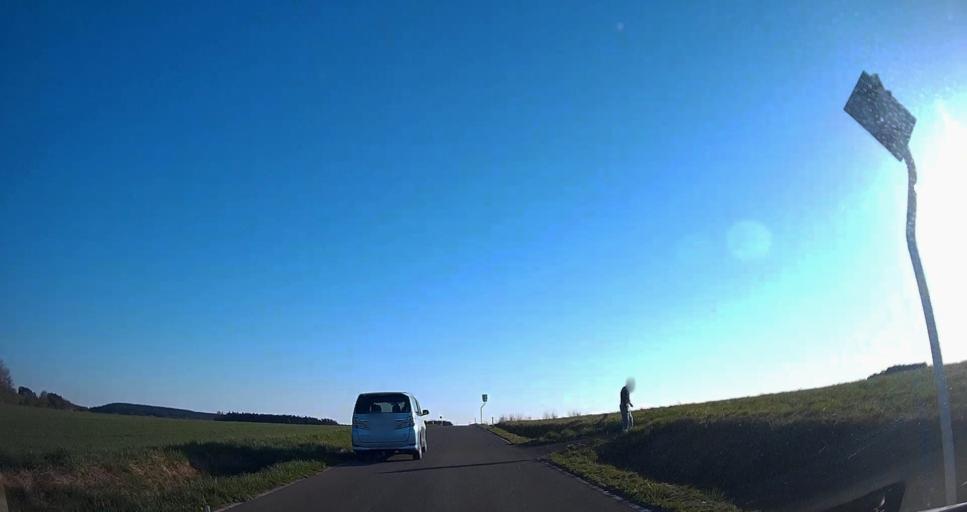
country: JP
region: Aomori
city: Mutsu
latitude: 41.1174
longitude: 141.2757
